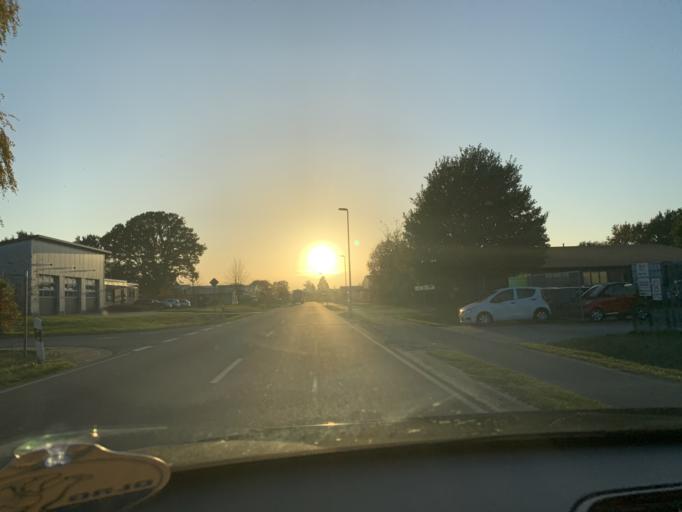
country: DE
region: Lower Saxony
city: Edewecht
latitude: 53.1216
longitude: 8.0009
